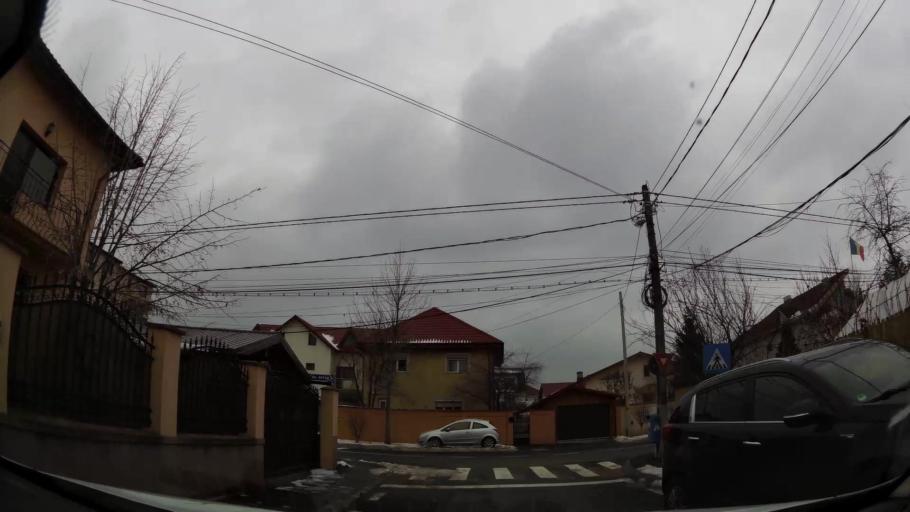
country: RO
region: Ilfov
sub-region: Comuna Otopeni
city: Otopeni
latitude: 44.5543
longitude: 26.0759
